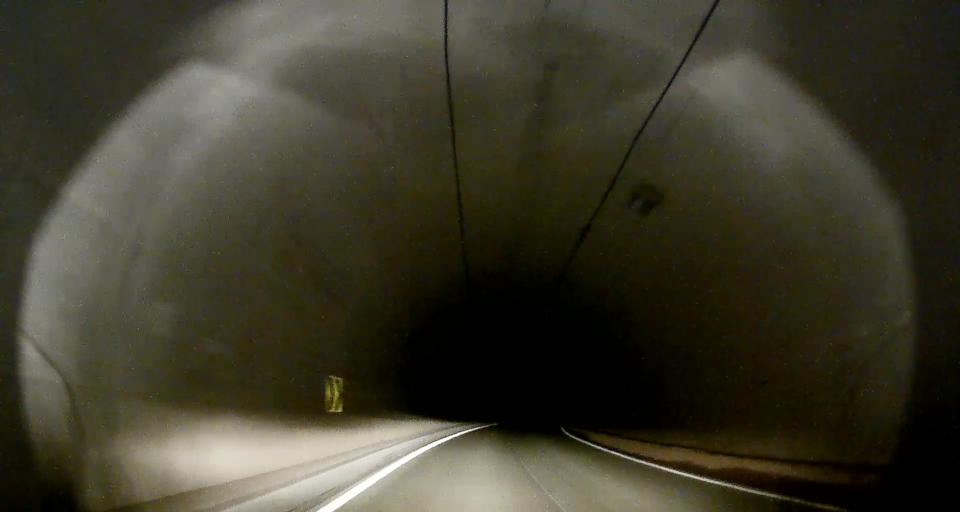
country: JP
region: Hokkaido
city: Chitose
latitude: 42.7888
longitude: 142.0449
